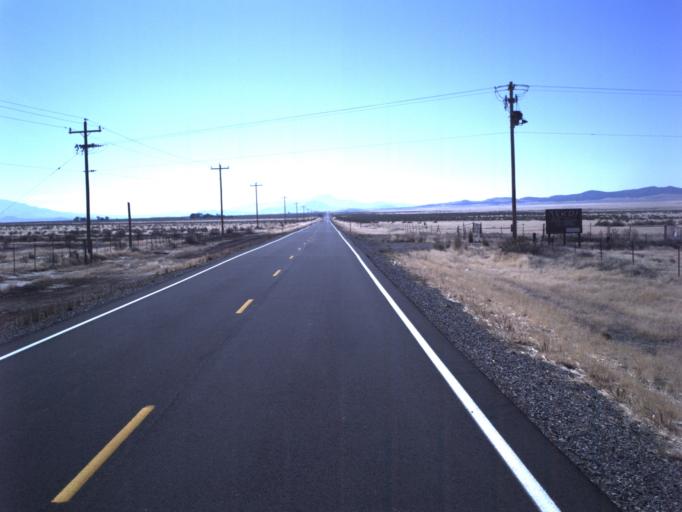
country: US
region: Utah
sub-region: Tooele County
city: Grantsville
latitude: 40.3698
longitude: -112.7464
